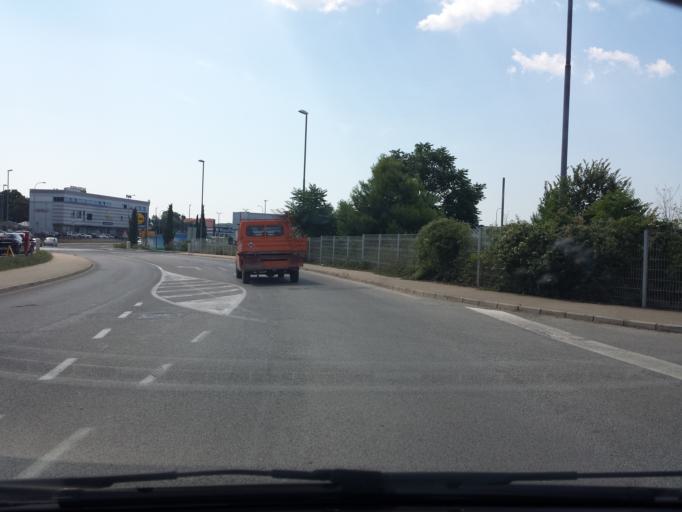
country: HR
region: Istarska
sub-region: Grad Pula
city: Pula
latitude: 44.8834
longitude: 13.8638
